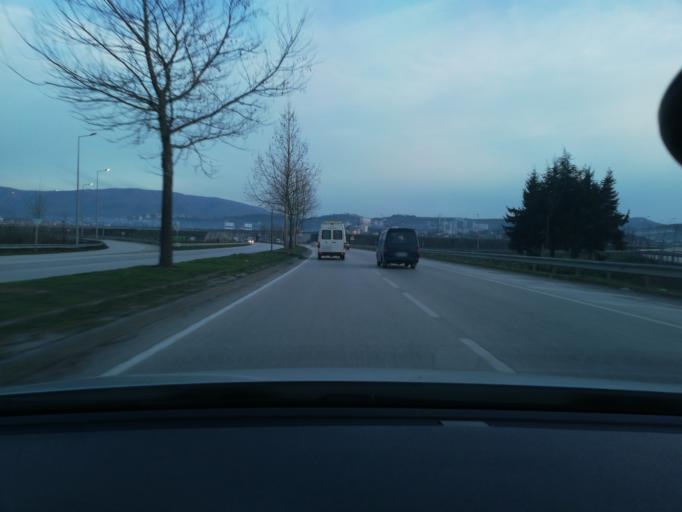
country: TR
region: Duzce
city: Konuralp
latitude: 40.8837
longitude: 31.1708
